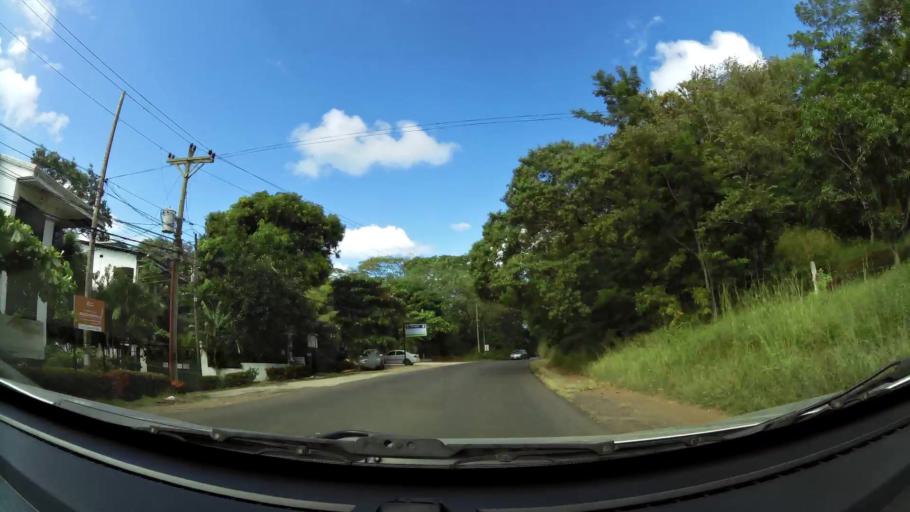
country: CR
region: Guanacaste
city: Santa Cruz
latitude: 10.3092
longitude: -85.8114
